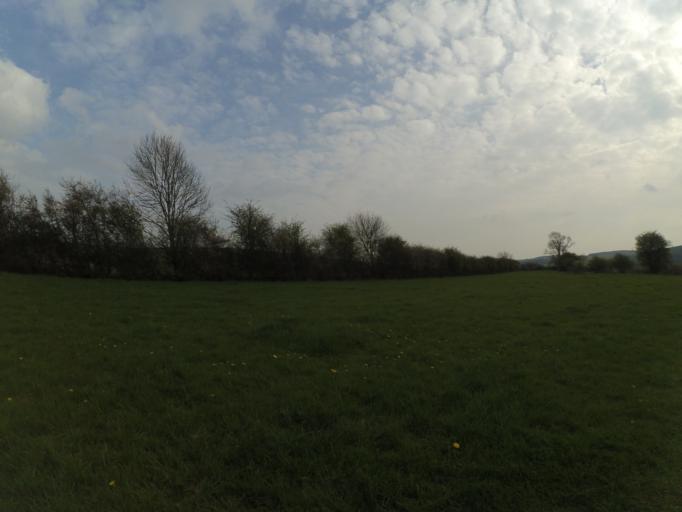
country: GB
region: England
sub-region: West Sussex
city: Arundel
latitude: 50.9078
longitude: -0.5480
